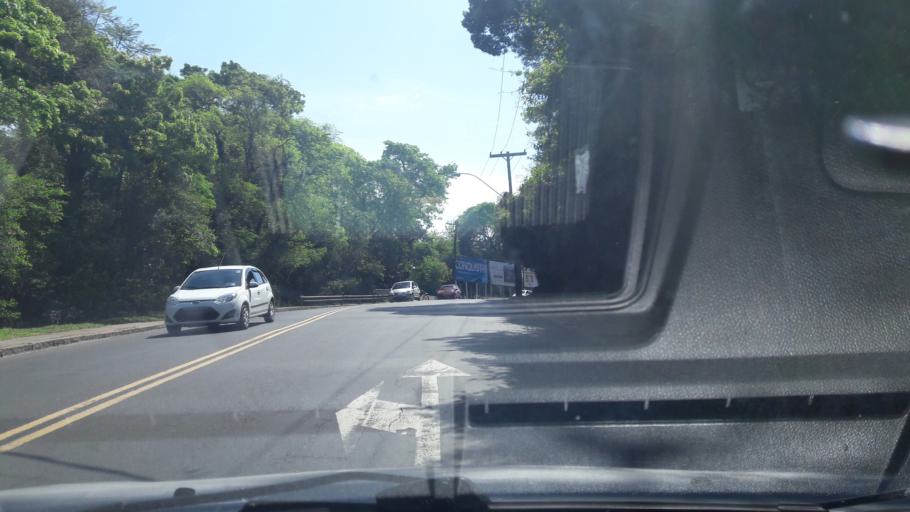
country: BR
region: Rio Grande do Sul
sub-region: Guaiba
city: Guaiba
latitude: -30.1204
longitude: -51.2534
